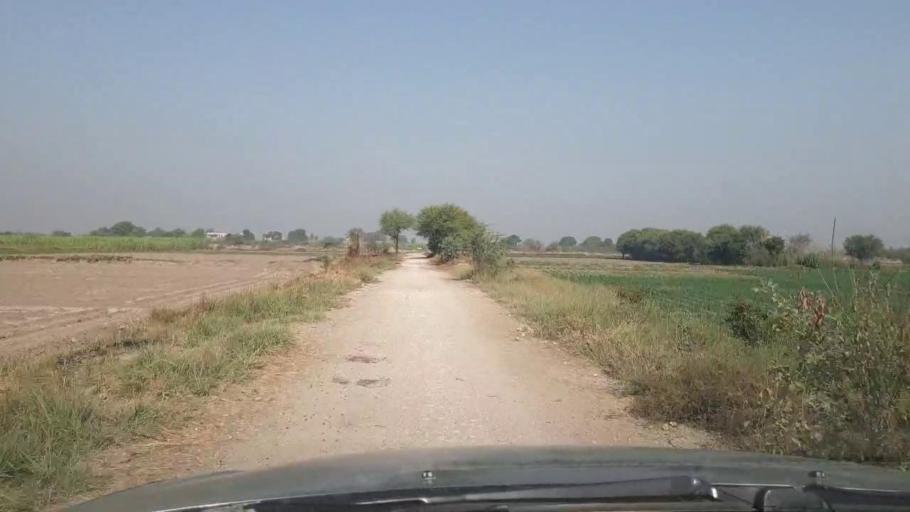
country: PK
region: Sindh
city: Tando Jam
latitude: 25.2845
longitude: 68.5334
